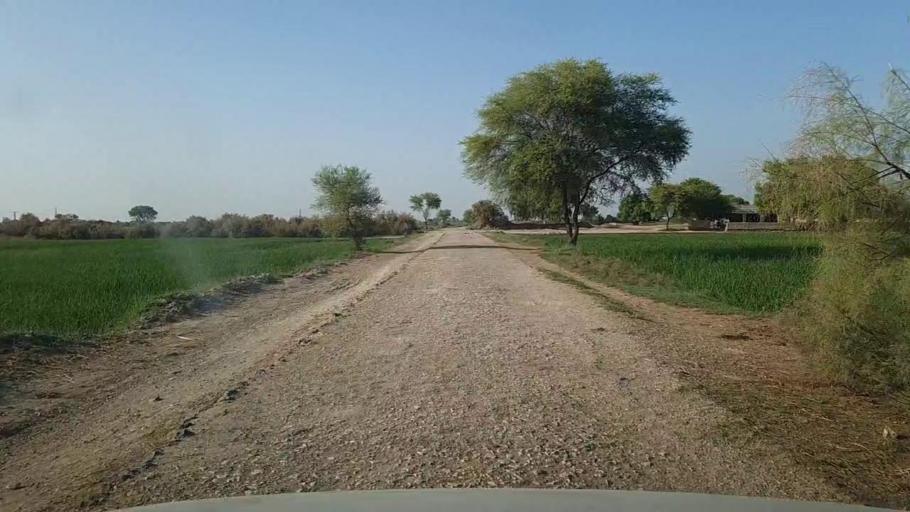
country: PK
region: Sindh
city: Kandhkot
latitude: 28.2996
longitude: 69.3288
